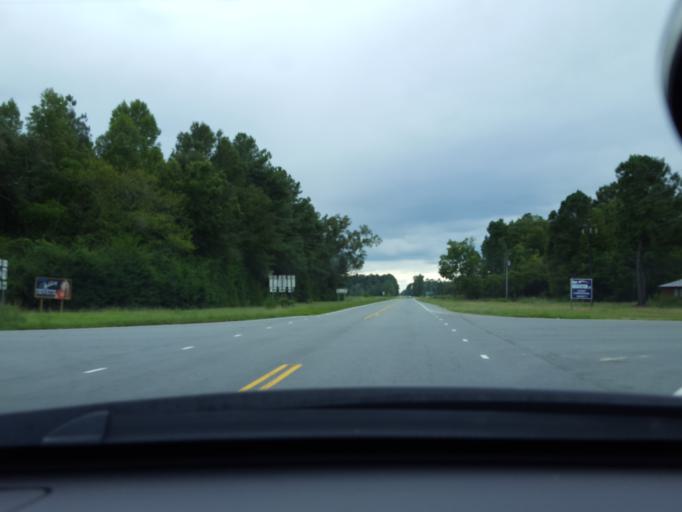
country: US
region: North Carolina
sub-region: Bladen County
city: Elizabethtown
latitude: 34.7485
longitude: -78.4215
